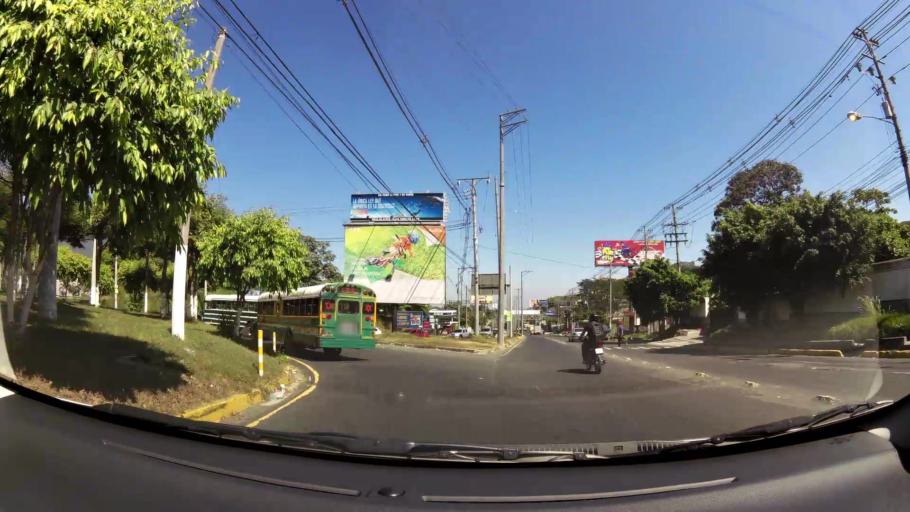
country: SV
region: La Libertad
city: Santa Tecla
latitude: 13.6629
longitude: -89.2777
